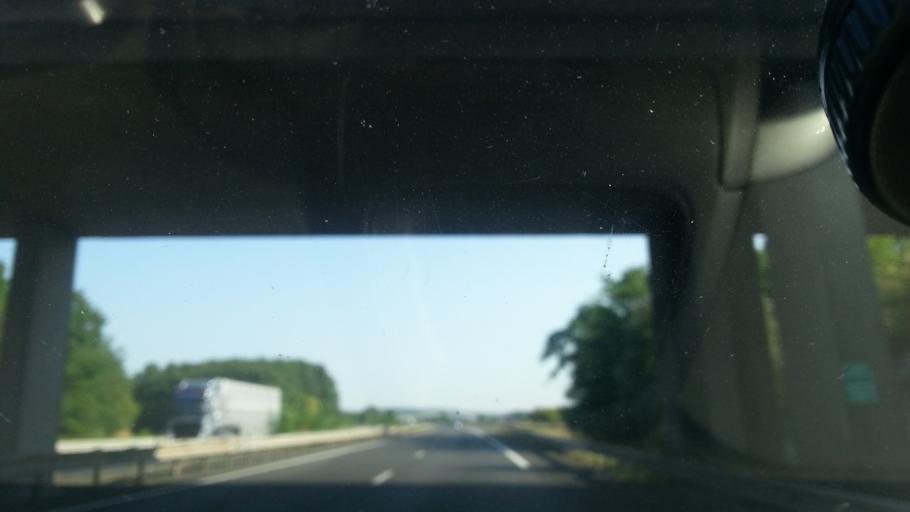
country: FR
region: Poitou-Charentes
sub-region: Departement de la Vienne
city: Antran
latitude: 46.8376
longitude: 0.5247
